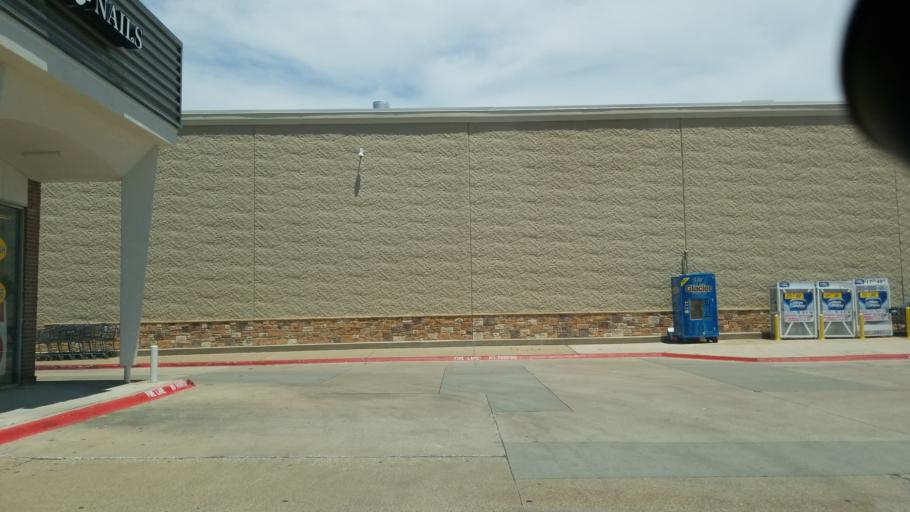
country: US
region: Texas
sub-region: Dallas County
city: Irving
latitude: 32.8296
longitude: -96.9753
